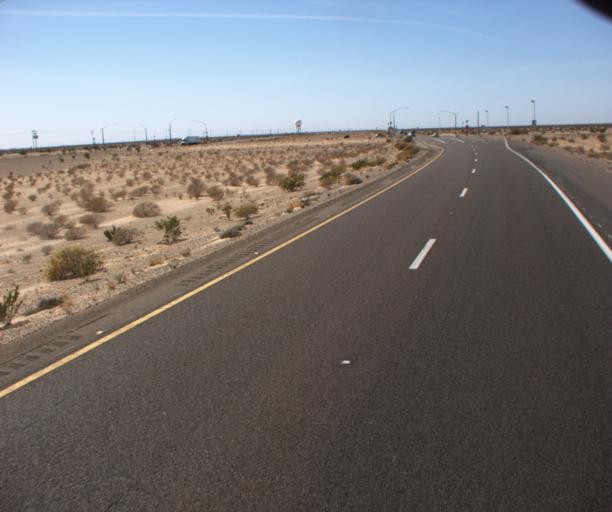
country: US
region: Arizona
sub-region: Yuma County
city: Somerton
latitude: 32.4967
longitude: -114.6454
